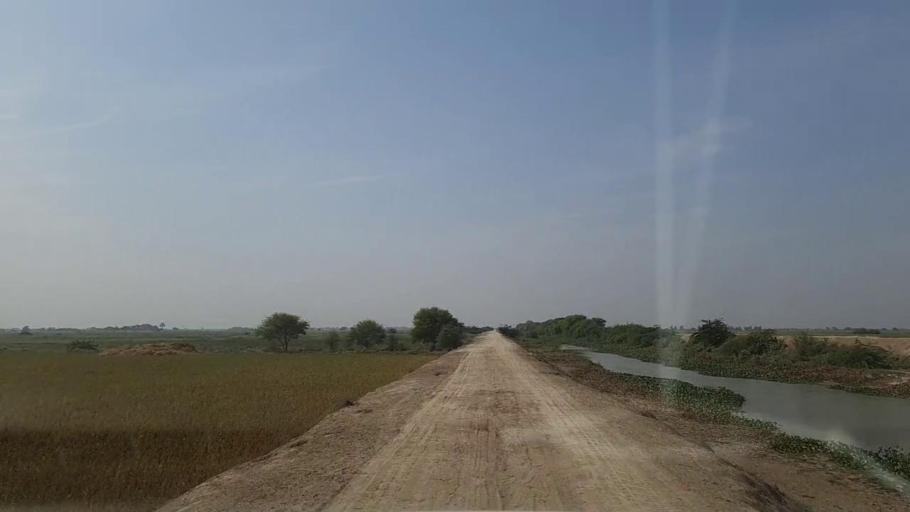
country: PK
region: Sindh
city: Mirpur Batoro
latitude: 24.6549
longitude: 68.2443
